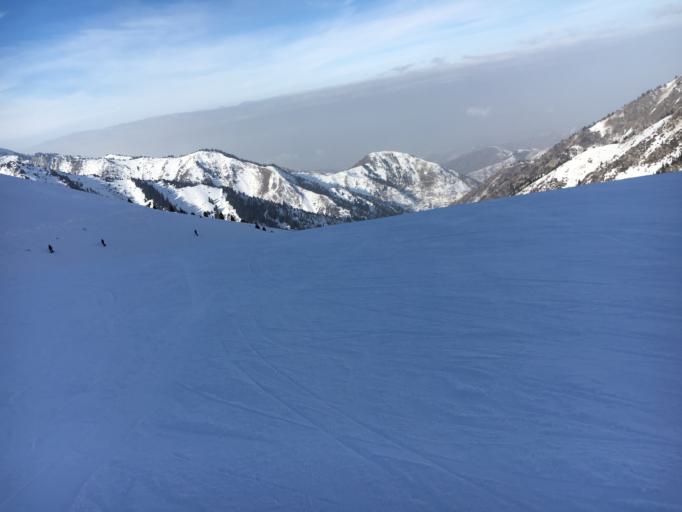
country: KZ
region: Almaty Qalasy
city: Almaty
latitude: 43.1190
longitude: 77.0977
